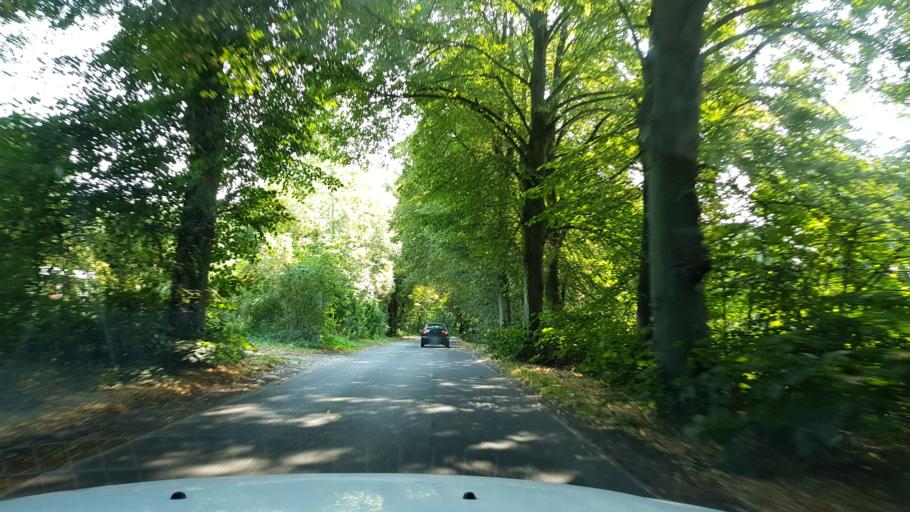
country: PL
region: West Pomeranian Voivodeship
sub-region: Powiat gryfinski
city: Chojna
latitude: 52.9536
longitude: 14.5021
